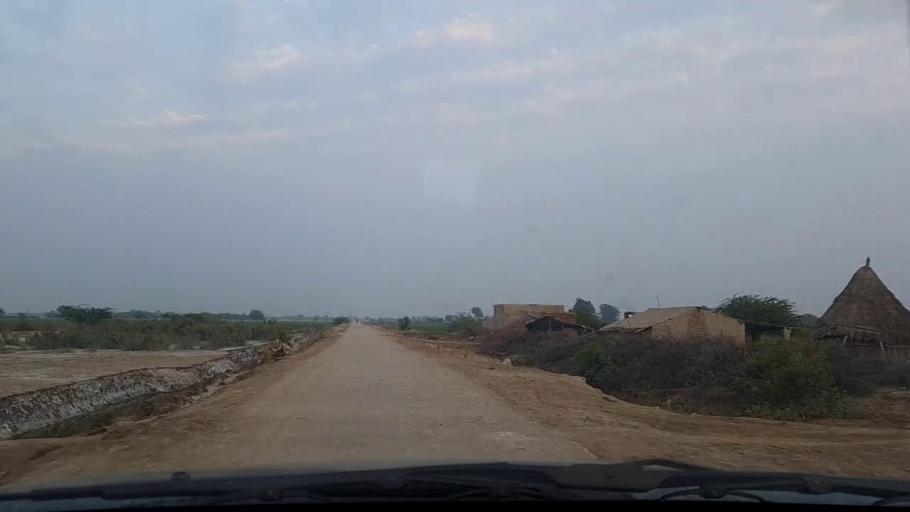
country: PK
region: Sindh
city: Pithoro
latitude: 25.6284
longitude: 69.4351
